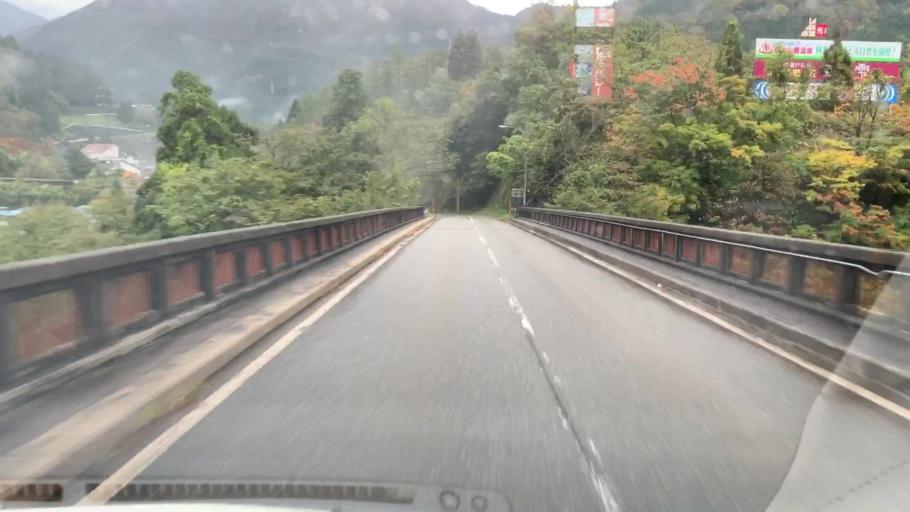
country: JP
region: Toyama
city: Kamiichi
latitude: 36.5742
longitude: 137.3779
